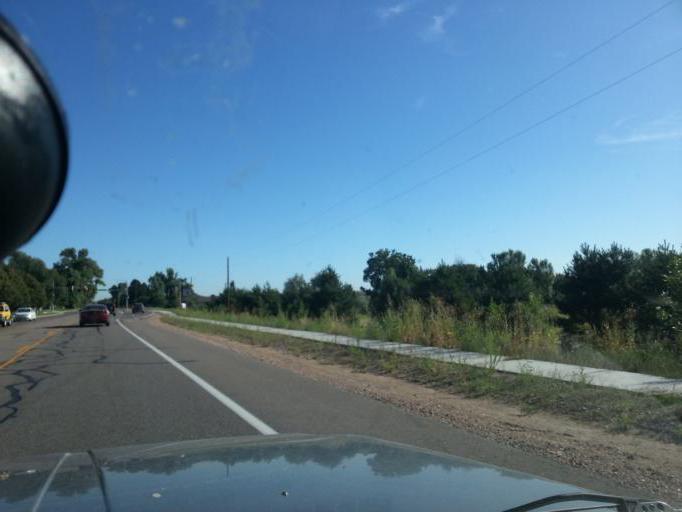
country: US
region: Colorado
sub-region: Larimer County
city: Fort Collins
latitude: 40.5076
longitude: -105.0393
